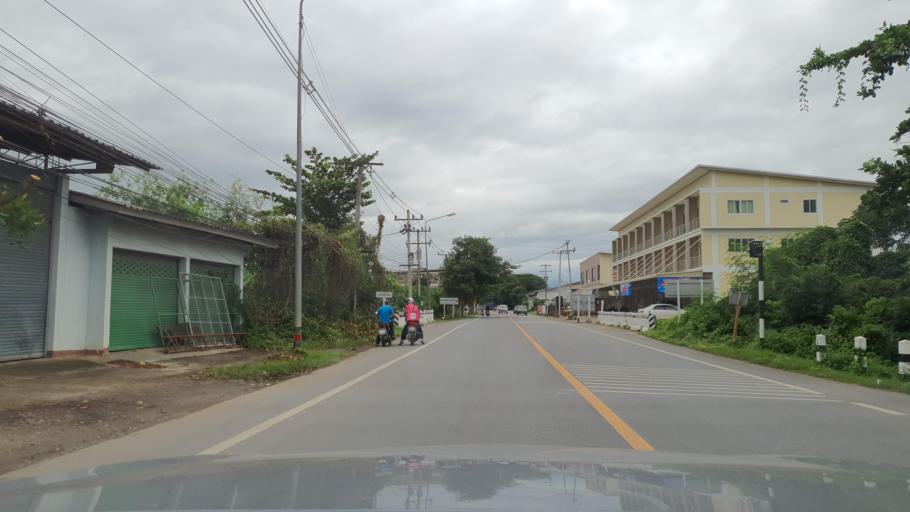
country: TH
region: Lamphun
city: Lamphun
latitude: 18.5917
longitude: 98.9786
